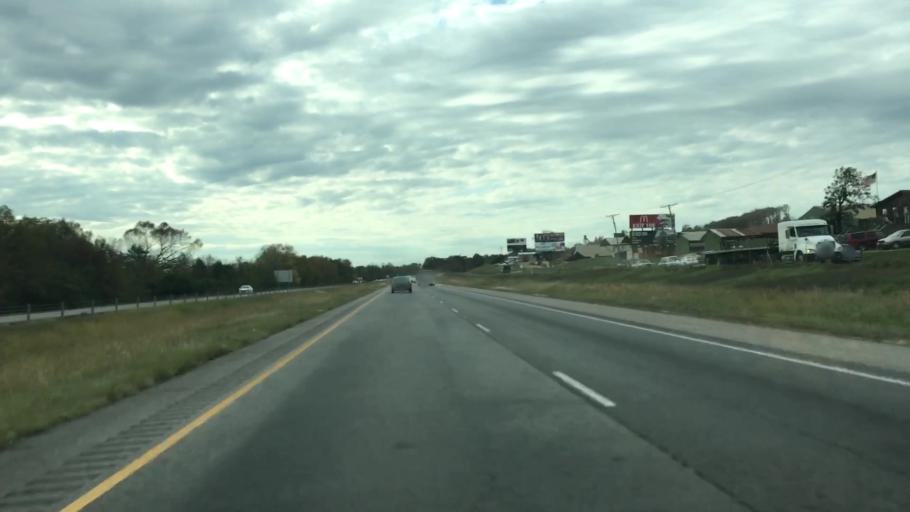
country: US
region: Arkansas
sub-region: Conway County
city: Morrilton
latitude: 35.1627
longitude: -92.6628
